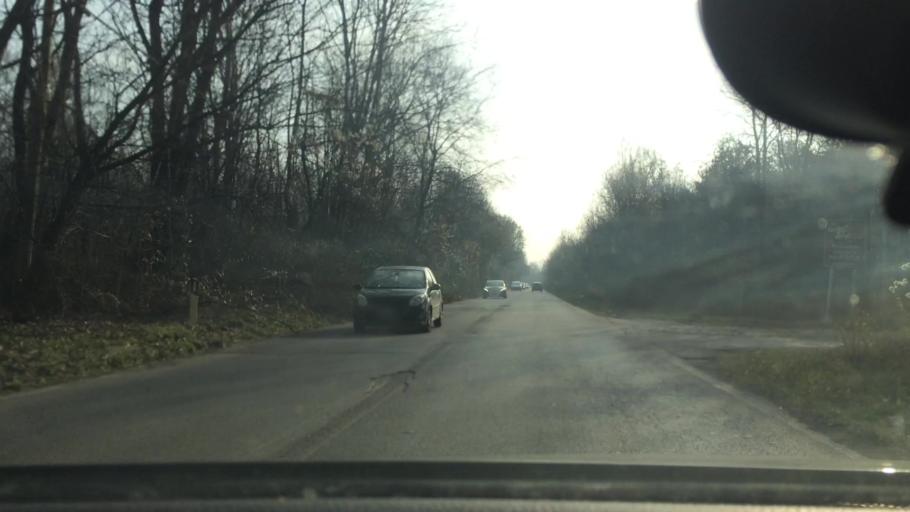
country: IT
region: Lombardy
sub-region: Provincia di Monza e Brianza
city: Villaggio del Sole
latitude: 45.6027
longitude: 9.0961
